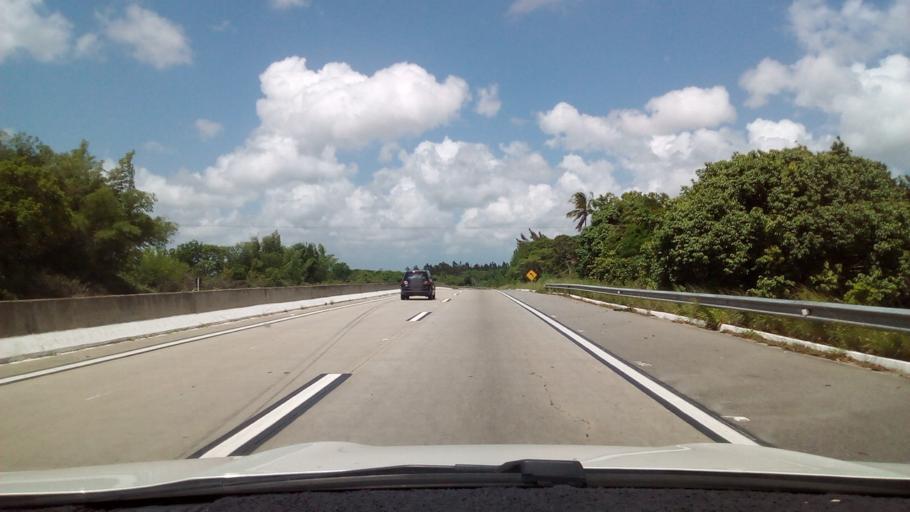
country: BR
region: Paraiba
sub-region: Conde
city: Conde
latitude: -7.3008
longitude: -34.9390
